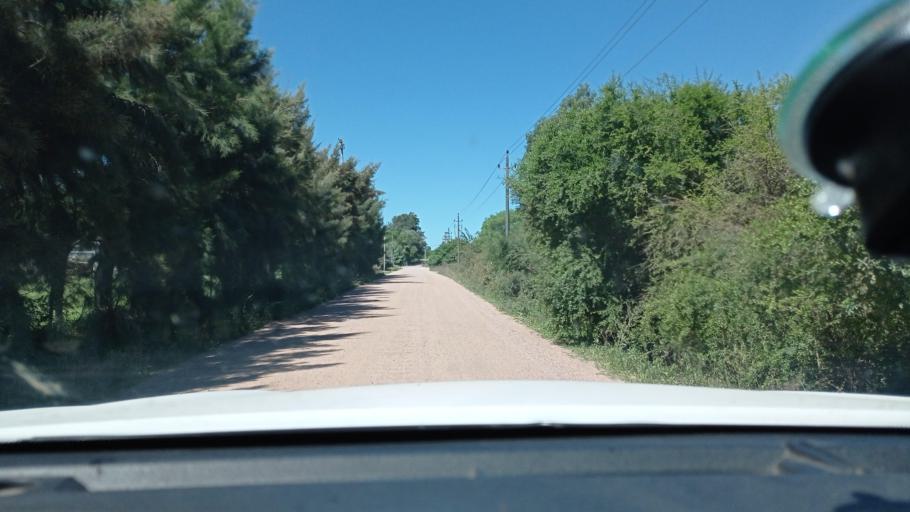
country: UY
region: Canelones
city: La Paz
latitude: -34.7596
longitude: -56.1674
